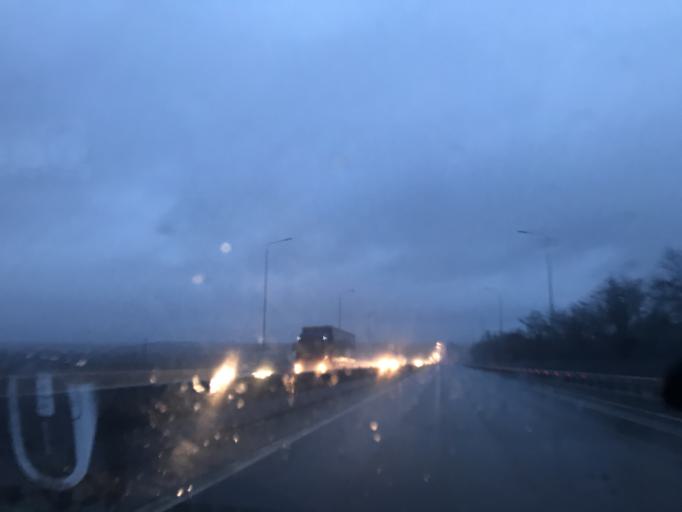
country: RU
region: Rostov
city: Samarskoye
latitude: 46.9909
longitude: 39.7271
